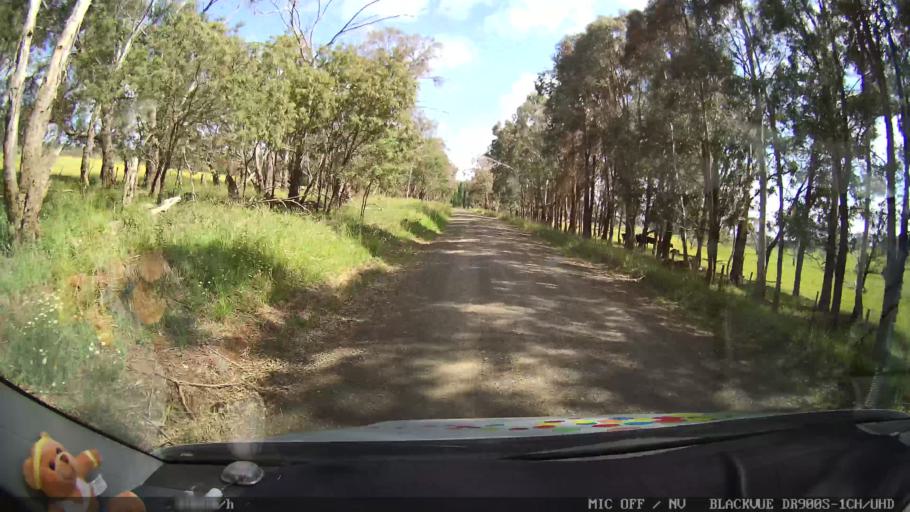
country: AU
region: New South Wales
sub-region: Glen Innes Severn
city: Glen Innes
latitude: -29.9668
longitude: 151.6993
